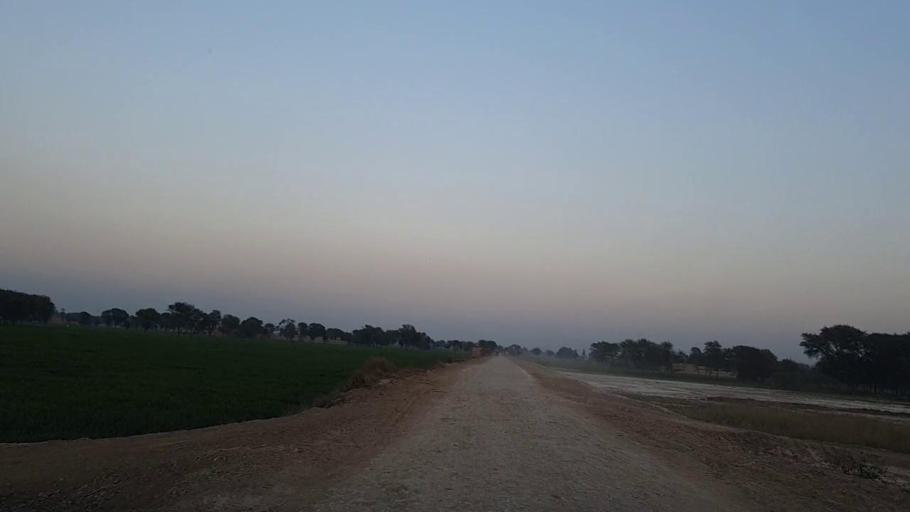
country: PK
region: Sindh
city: Naushahro Firoz
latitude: 26.8005
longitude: 68.0178
